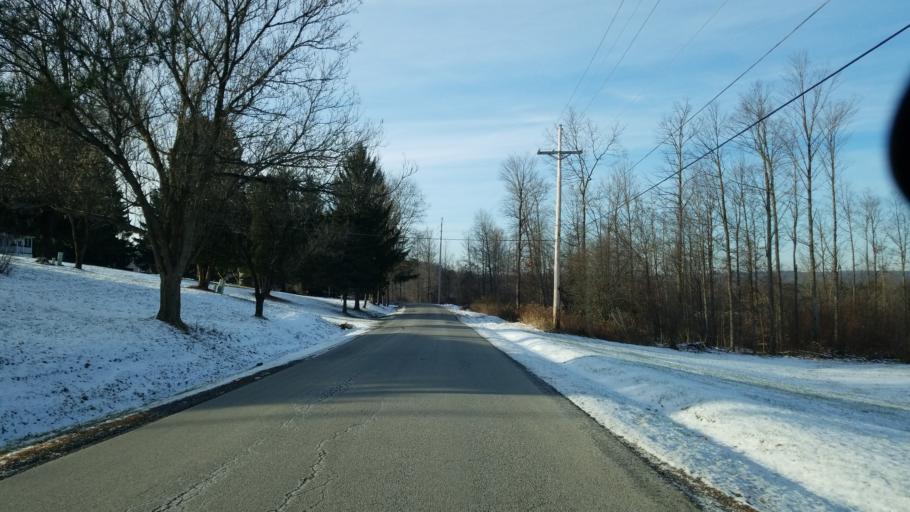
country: US
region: Pennsylvania
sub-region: Clearfield County
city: DuBois
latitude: 41.1112
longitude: -78.7002
